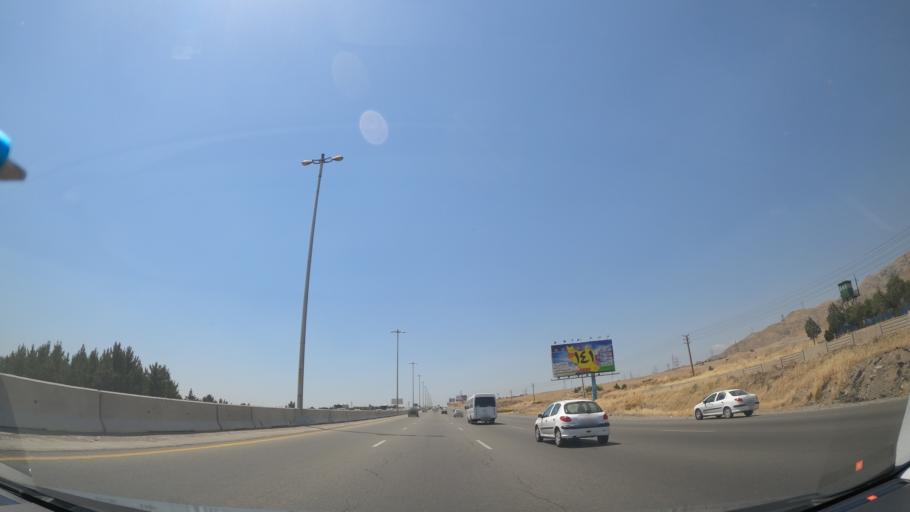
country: IR
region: Tehran
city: Shahr-e Qods
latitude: 35.7650
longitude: 51.0567
